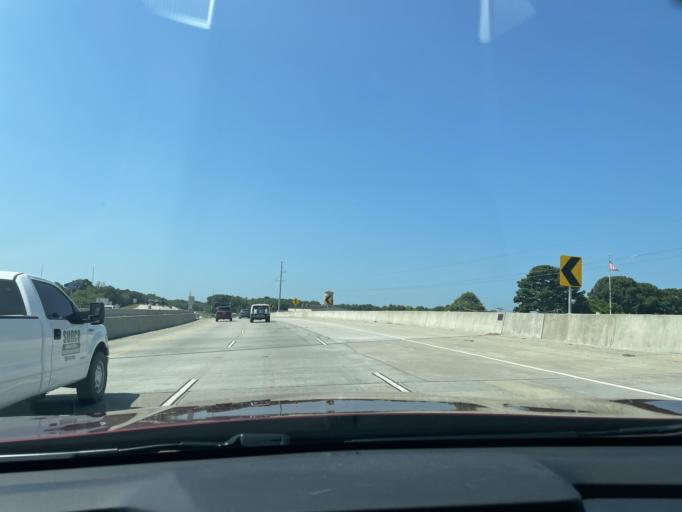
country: US
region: Arkansas
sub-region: Pulaski County
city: Jacksonville
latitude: 34.8680
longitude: -92.1276
